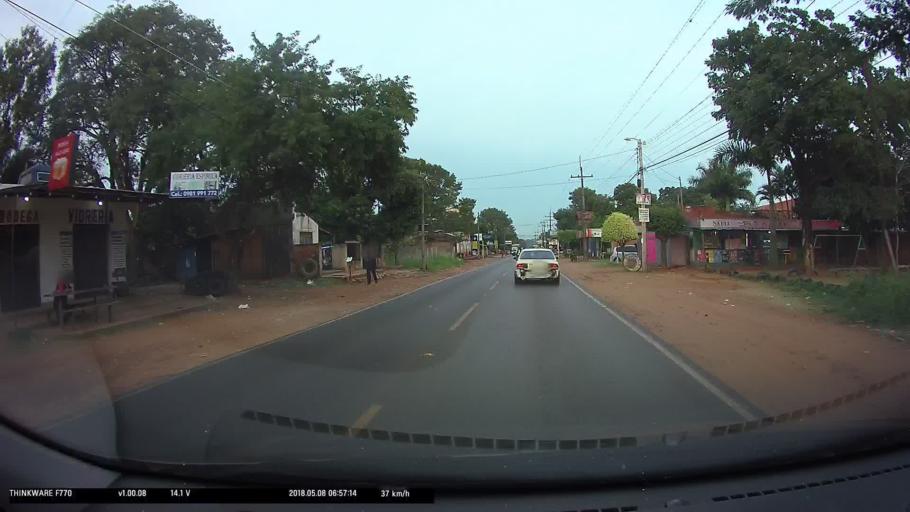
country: PY
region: Central
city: Limpio
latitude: -25.2423
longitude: -57.4771
